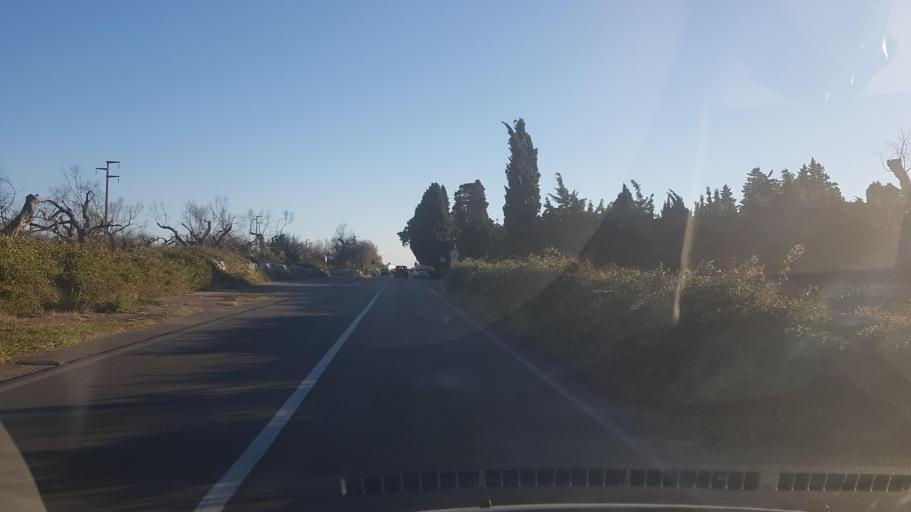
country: IT
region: Apulia
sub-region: Provincia di Lecce
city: Struda
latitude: 40.3276
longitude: 18.2889
